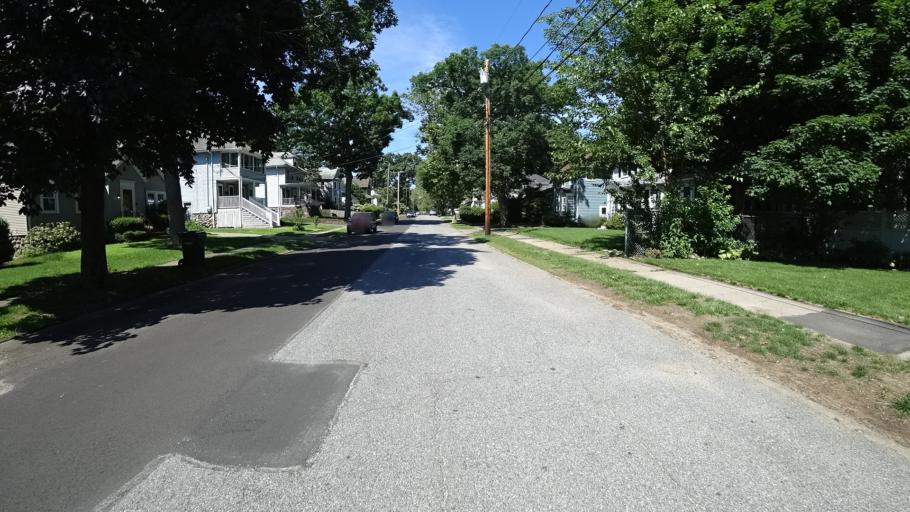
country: US
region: Massachusetts
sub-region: Norfolk County
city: Dedham
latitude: 42.2412
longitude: -71.1567
